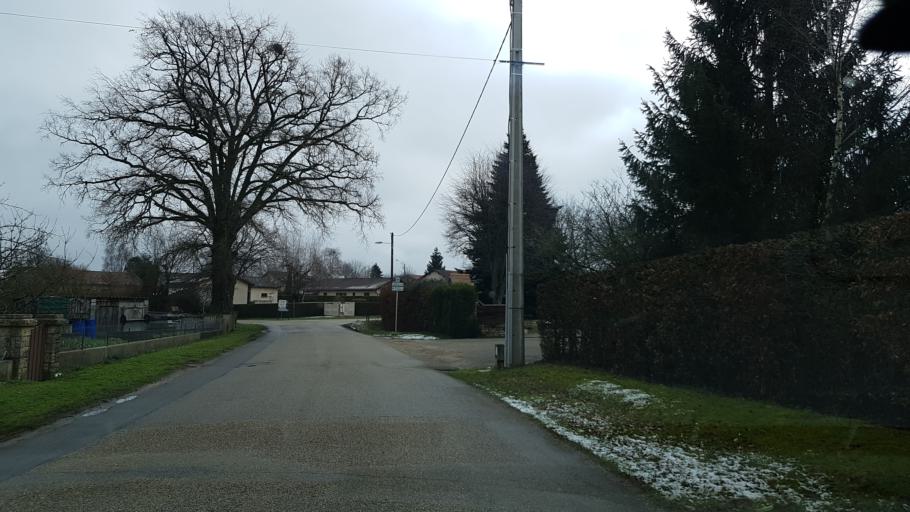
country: FR
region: Rhone-Alpes
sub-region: Departement de l'Ain
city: Saint-Denis-les-Bourg
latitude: 46.1865
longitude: 5.1654
